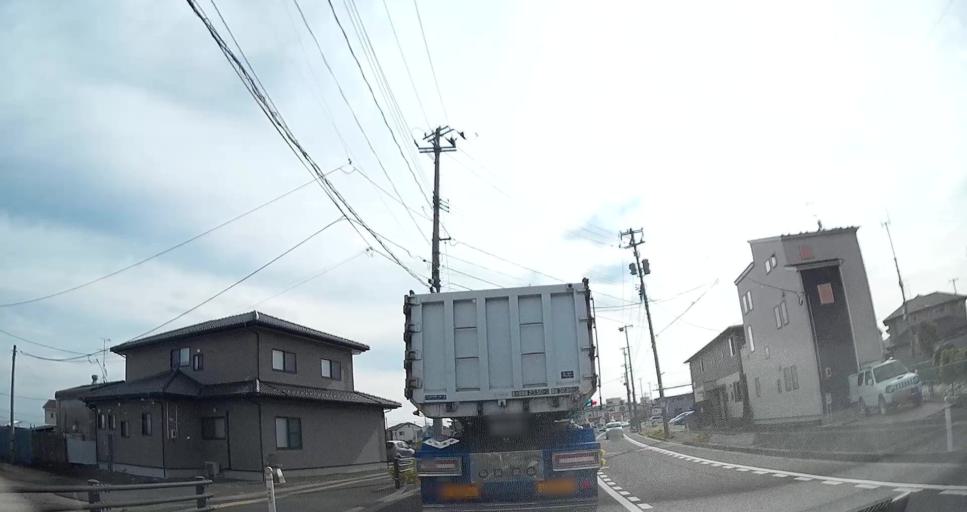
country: JP
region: Miyagi
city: Sendai
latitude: 38.2175
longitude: 140.9305
